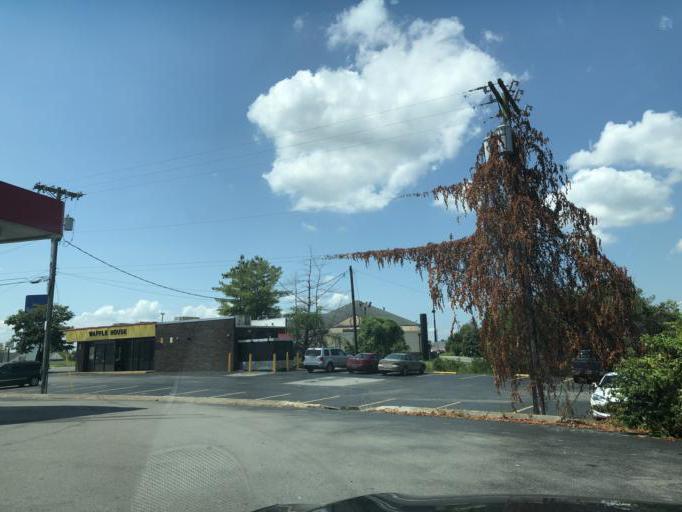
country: US
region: Tennessee
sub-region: Montgomery County
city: Clarksville
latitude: 36.5256
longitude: -87.2254
